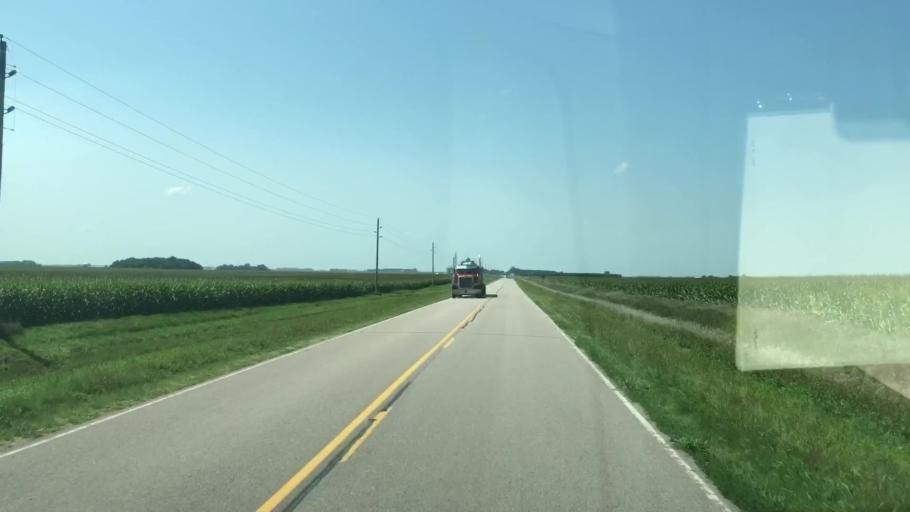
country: US
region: Iowa
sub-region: O'Brien County
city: Sheldon
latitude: 43.2443
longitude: -95.7871
